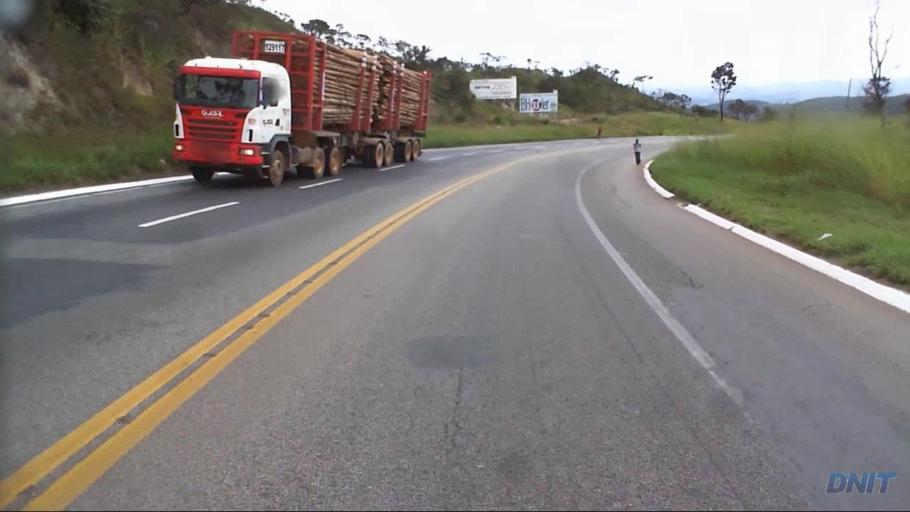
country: BR
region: Minas Gerais
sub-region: Caete
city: Caete
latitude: -19.7880
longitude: -43.7091
